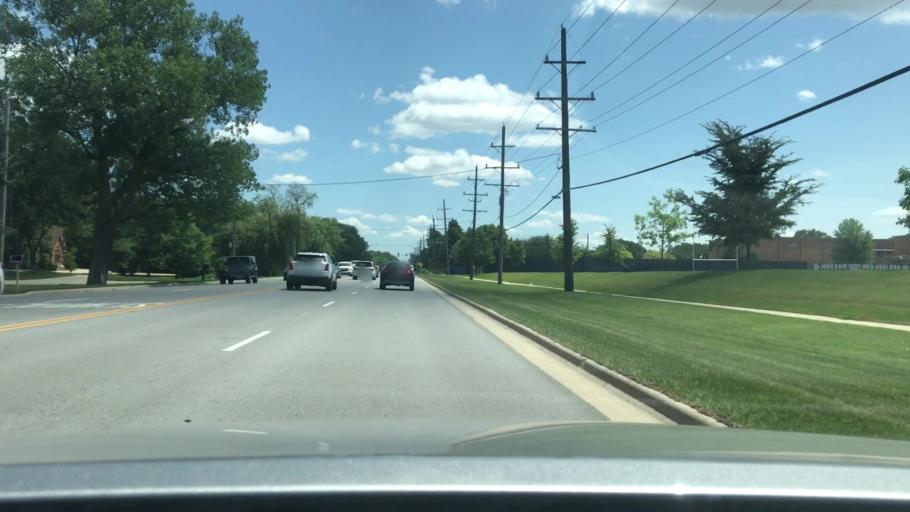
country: US
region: Illinois
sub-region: DuPage County
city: Woodridge
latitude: 41.7727
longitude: -88.0231
